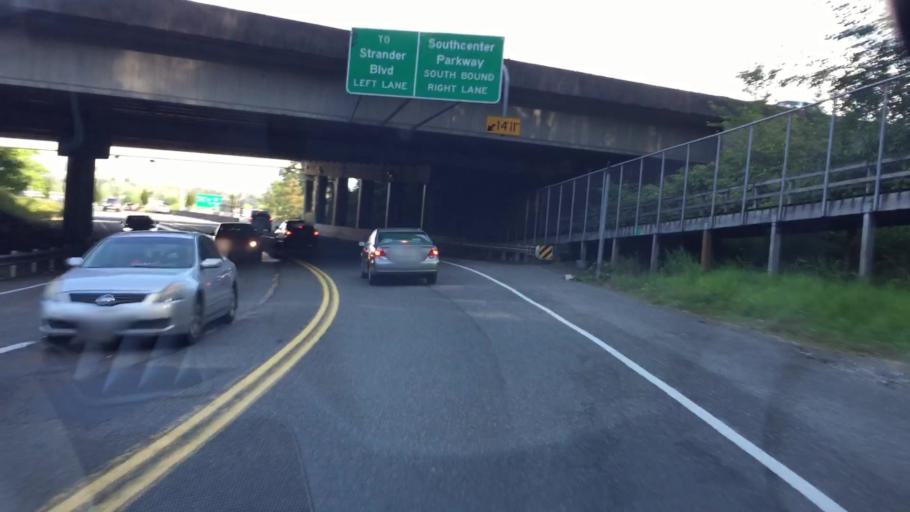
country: US
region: Washington
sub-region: King County
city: Tukwila
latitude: 47.4579
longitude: -122.2649
